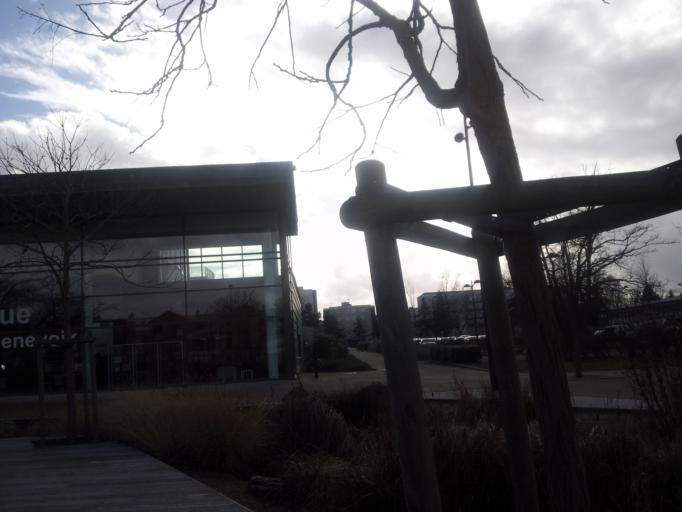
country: FR
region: Centre
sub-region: Departement du Loiret
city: Saint-Cyr-en-Val
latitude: 47.8353
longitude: 1.9290
